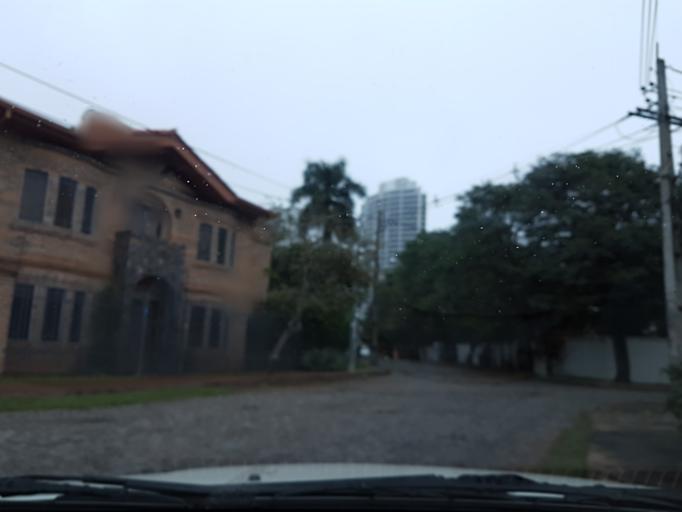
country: PY
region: Central
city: Fernando de la Mora
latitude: -25.2849
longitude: -57.5559
